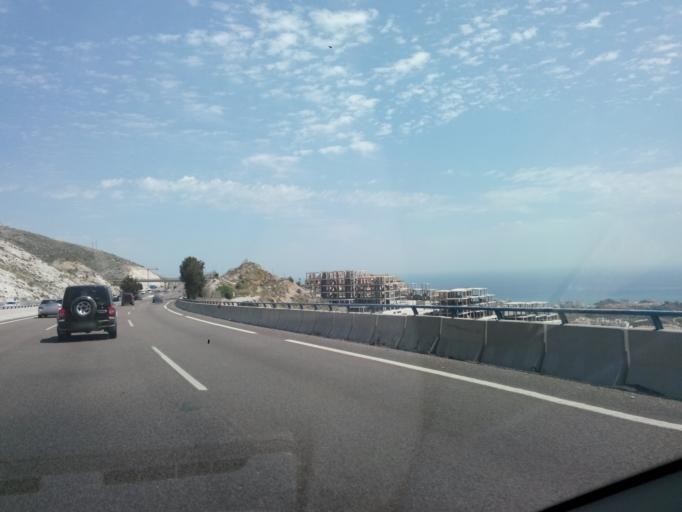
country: ES
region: Andalusia
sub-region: Provincia de Malaga
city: Benalmadena
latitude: 36.6046
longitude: -4.5660
